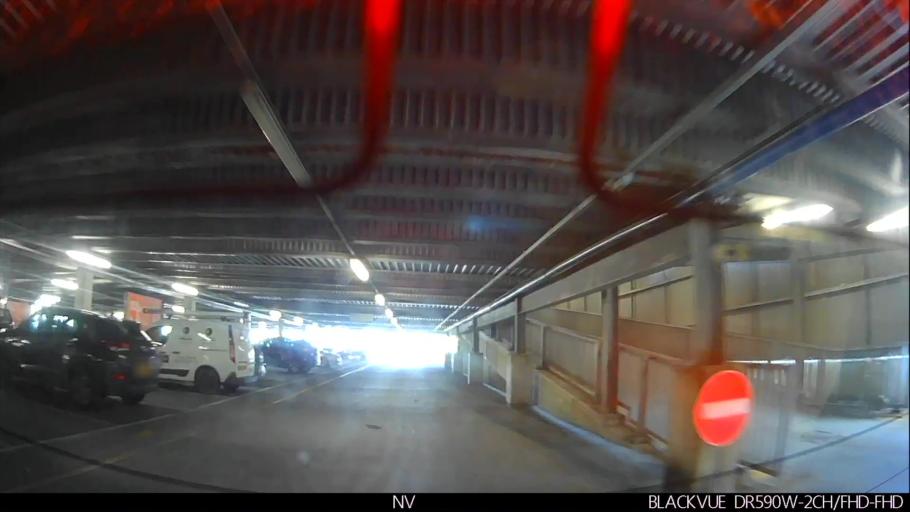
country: GB
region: England
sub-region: City and Borough of Leeds
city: Drighlington
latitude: 53.7434
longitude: -1.6477
